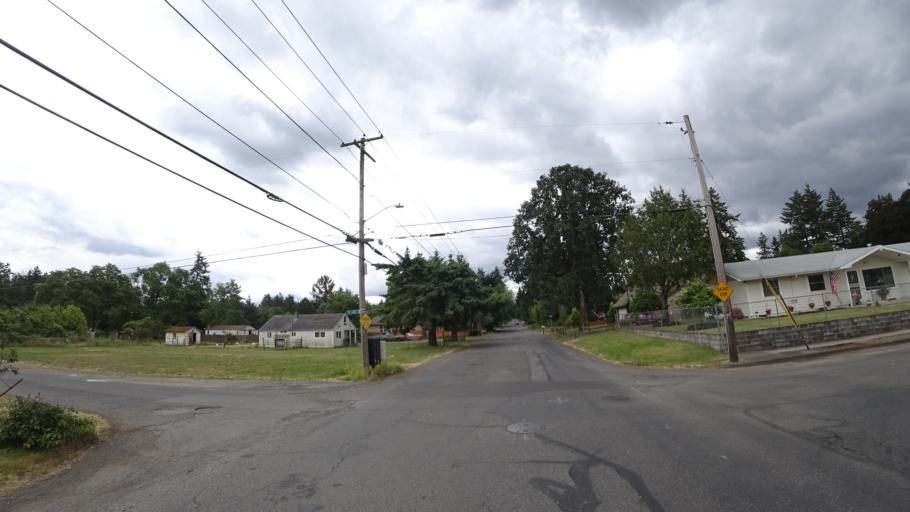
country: US
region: Oregon
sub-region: Multnomah County
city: Lents
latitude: 45.4880
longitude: -122.5323
